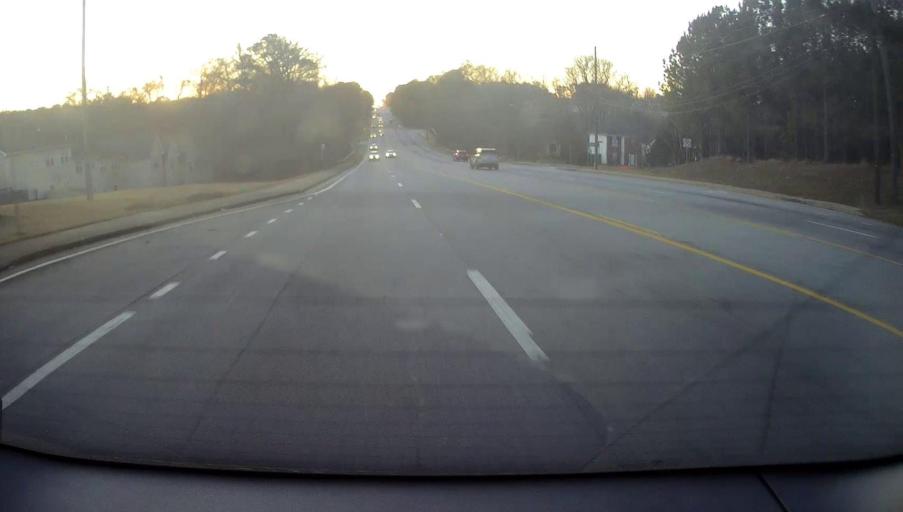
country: US
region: Georgia
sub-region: Clayton County
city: Riverdale
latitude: 33.5507
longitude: -84.4378
